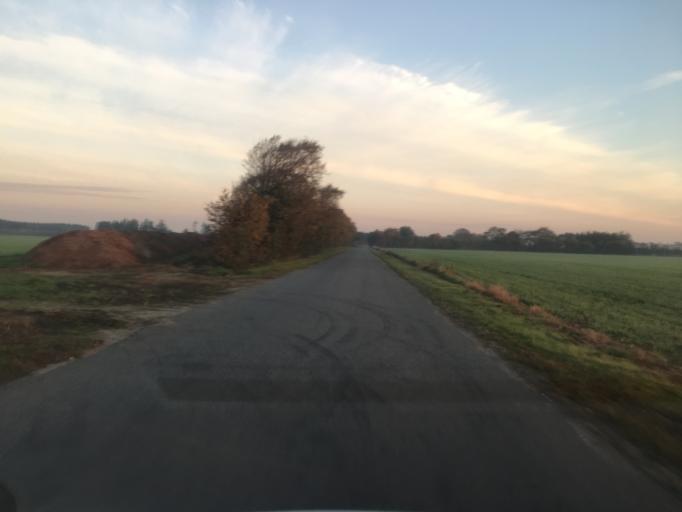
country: DK
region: South Denmark
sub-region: Tonder Kommune
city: Logumkloster
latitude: 55.0171
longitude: 9.0467
